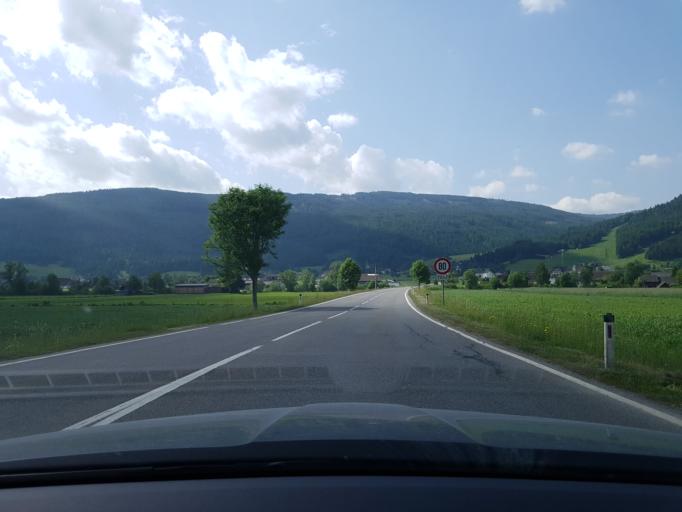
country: AT
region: Salzburg
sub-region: Politischer Bezirk Tamsweg
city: Sankt Margarethen im Lungau
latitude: 47.0905
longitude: 13.6923
